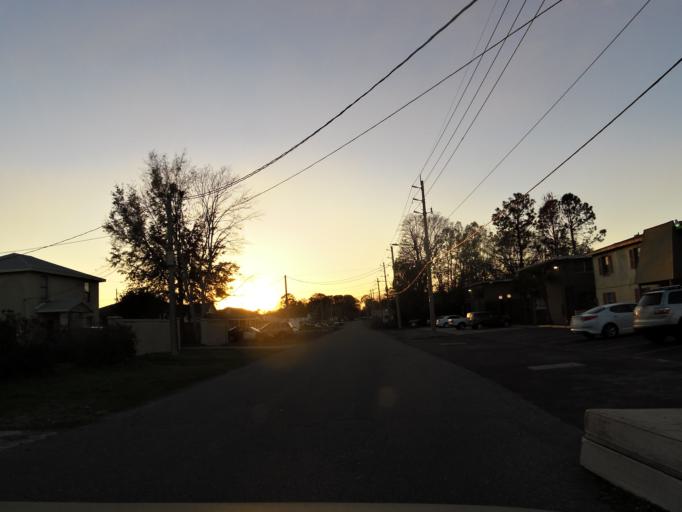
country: US
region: Florida
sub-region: Duval County
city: Jacksonville
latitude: 30.2831
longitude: -81.7225
